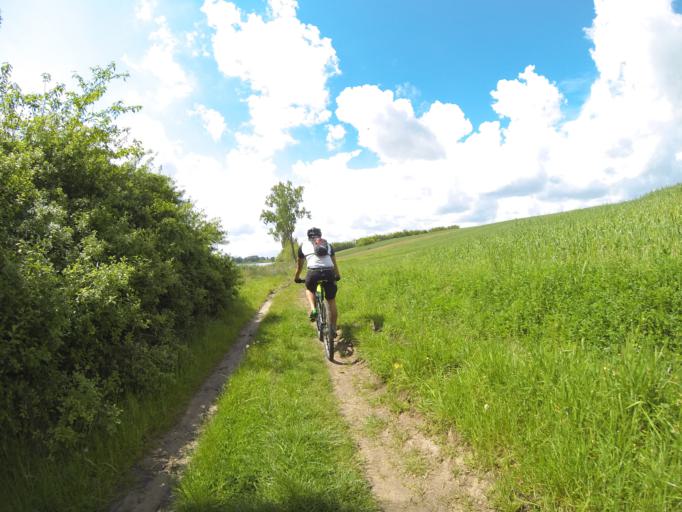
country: RO
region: Dolj
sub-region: Comuna Malu Mare
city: Preajba
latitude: 44.2657
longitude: 23.8567
